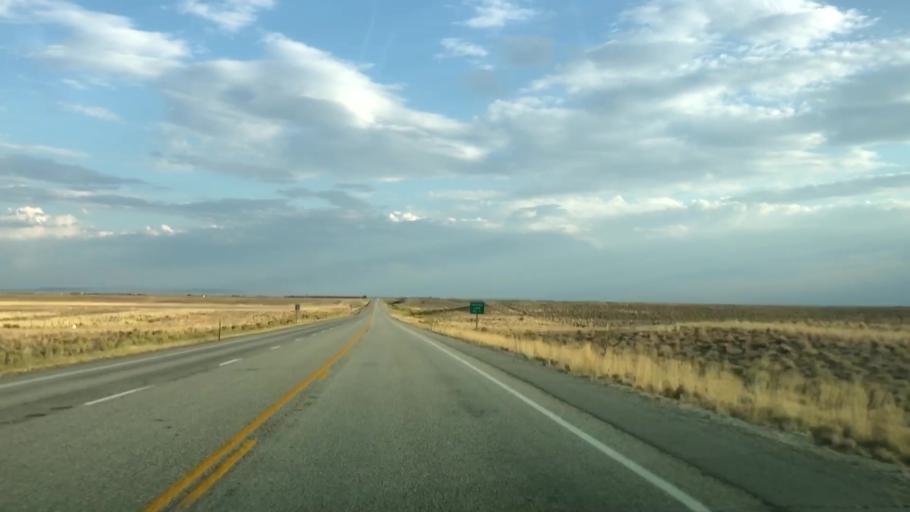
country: US
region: Wyoming
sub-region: Sweetwater County
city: North Rock Springs
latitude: 42.1883
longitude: -109.4800
